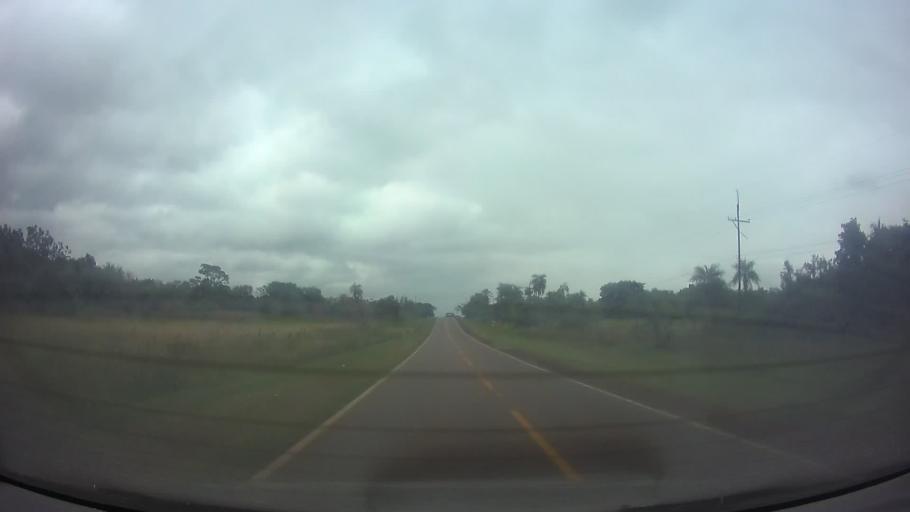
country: PY
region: Paraguari
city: Acahay
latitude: -25.8724
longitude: -57.1250
